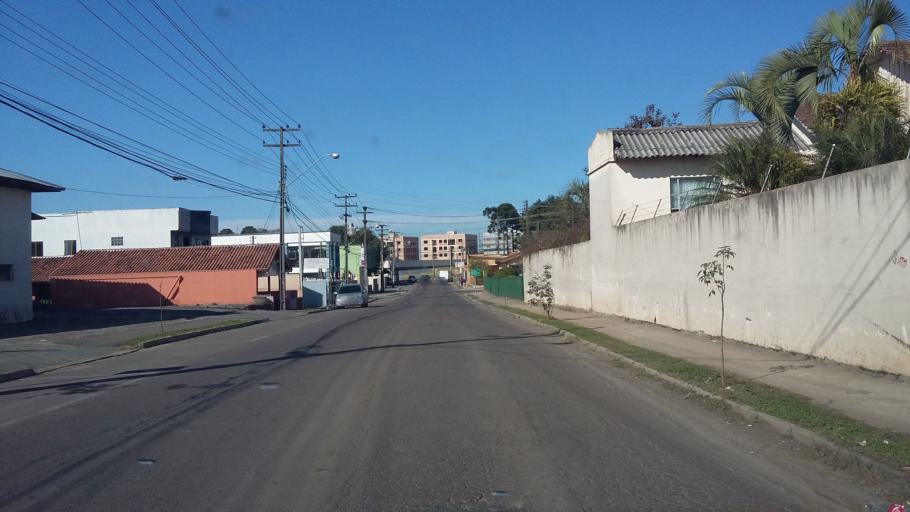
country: BR
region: Parana
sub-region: Campo Largo
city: Campo Largo
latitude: -25.4524
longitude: -49.5417
